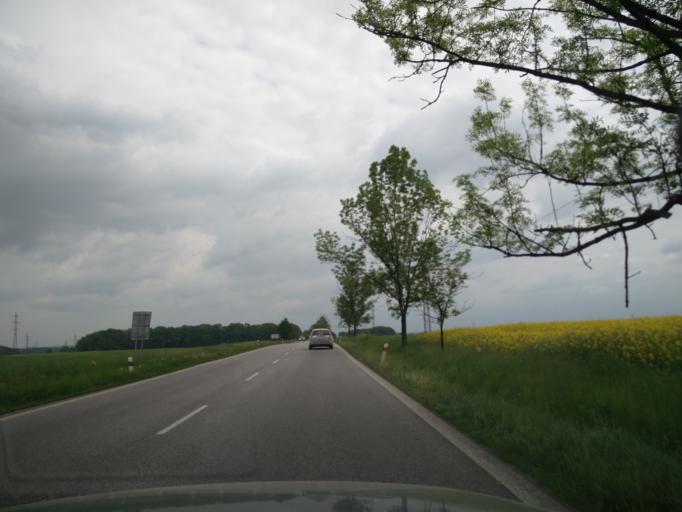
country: CZ
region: Jihocesky
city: Zliv
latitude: 49.0286
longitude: 14.3752
